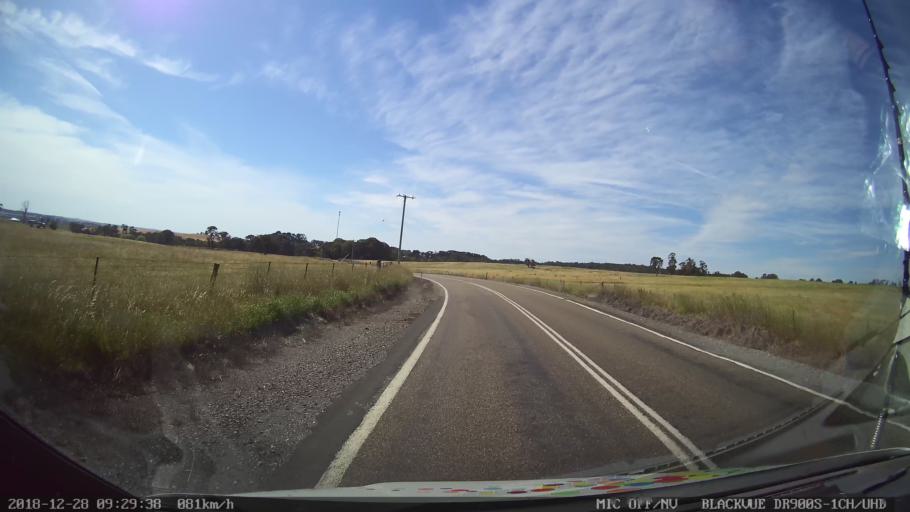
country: AU
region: New South Wales
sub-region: Upper Lachlan Shire
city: Crookwell
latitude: -34.4470
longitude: 149.4304
